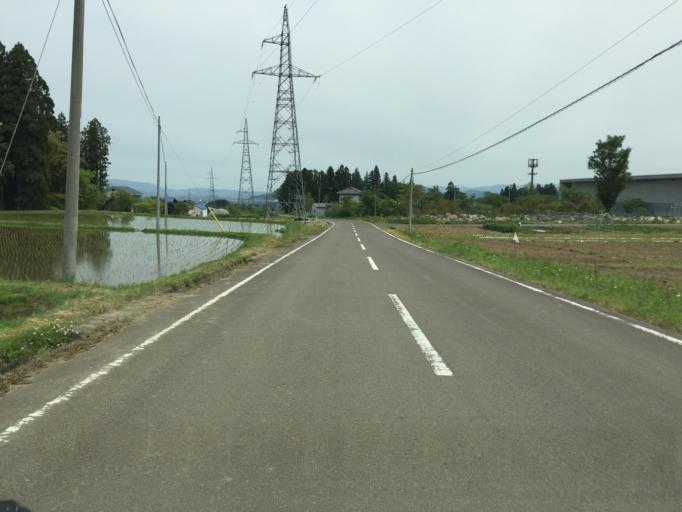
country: JP
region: Fukushima
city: Fukushima-shi
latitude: 37.7104
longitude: 140.3688
